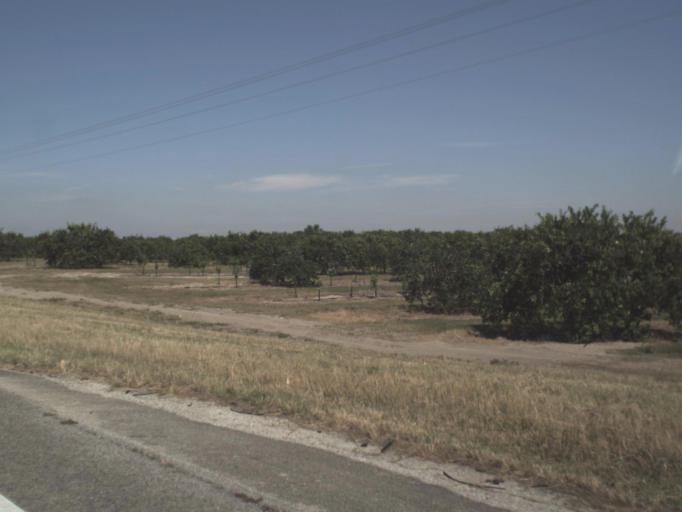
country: US
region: Florida
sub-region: Highlands County
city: Placid Lakes
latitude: 27.1900
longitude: -81.3285
